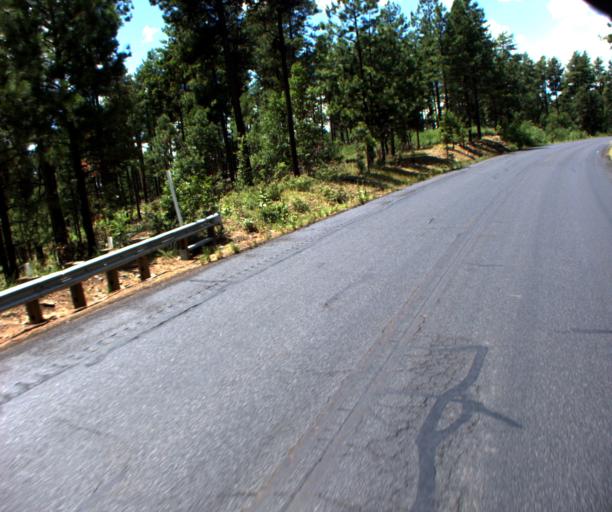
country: US
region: Arizona
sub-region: Gila County
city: Pine
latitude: 34.4655
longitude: -111.4453
